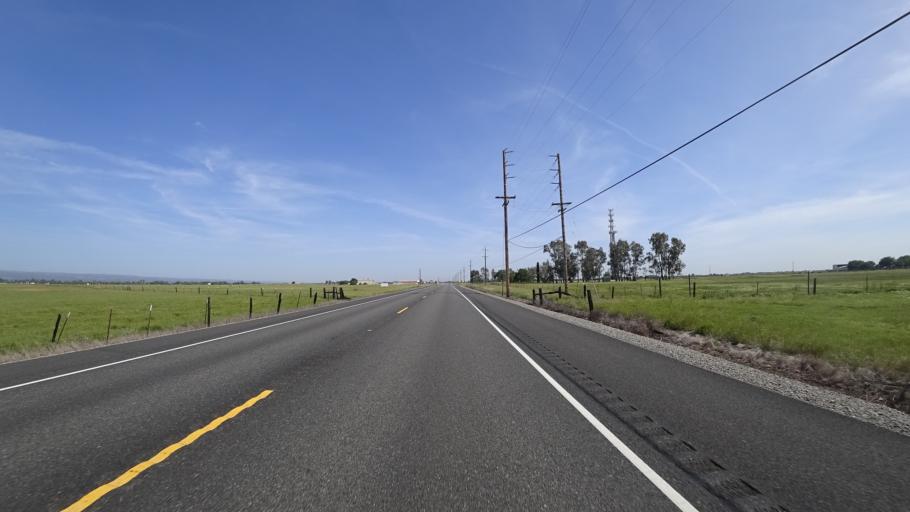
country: US
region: California
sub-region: Glenn County
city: Hamilton City
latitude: 39.8554
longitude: -121.9530
